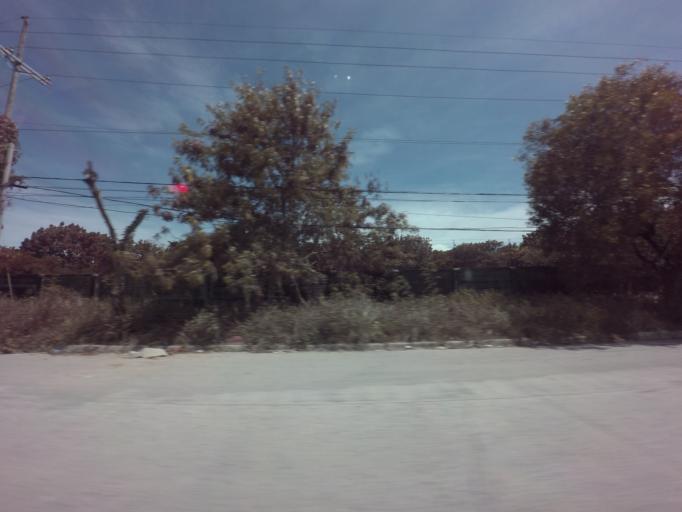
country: PH
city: Sambayanihan People's Village
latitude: 14.5076
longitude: 120.9838
